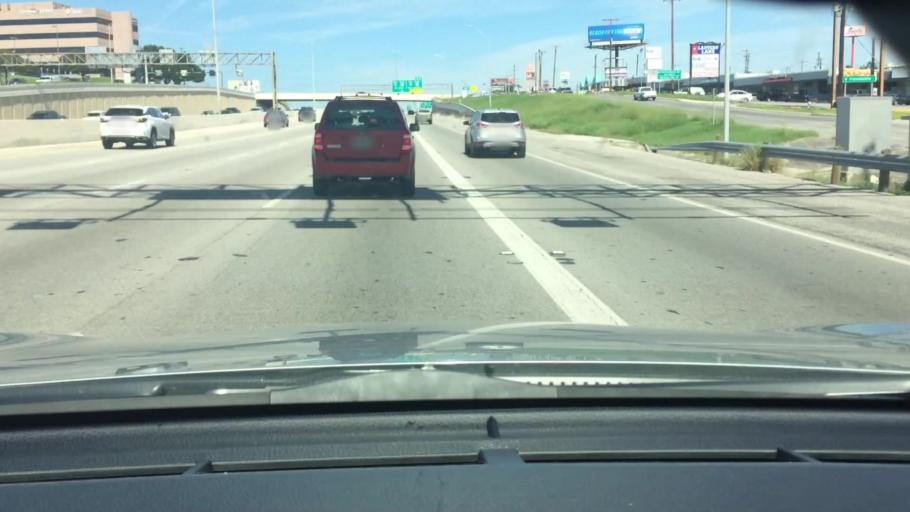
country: US
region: Texas
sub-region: Bexar County
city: Balcones Heights
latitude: 29.4921
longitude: -98.5557
